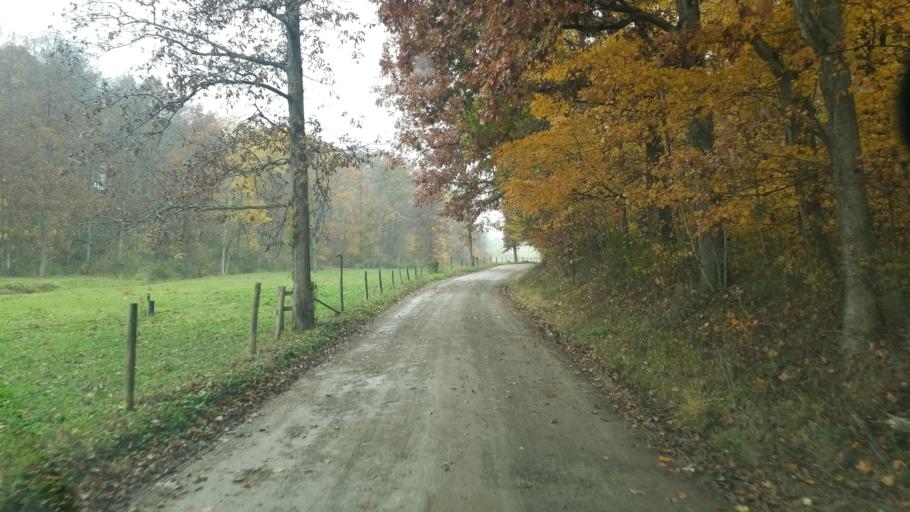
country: US
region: Ohio
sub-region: Holmes County
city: Millersburg
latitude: 40.4320
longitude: -81.8177
